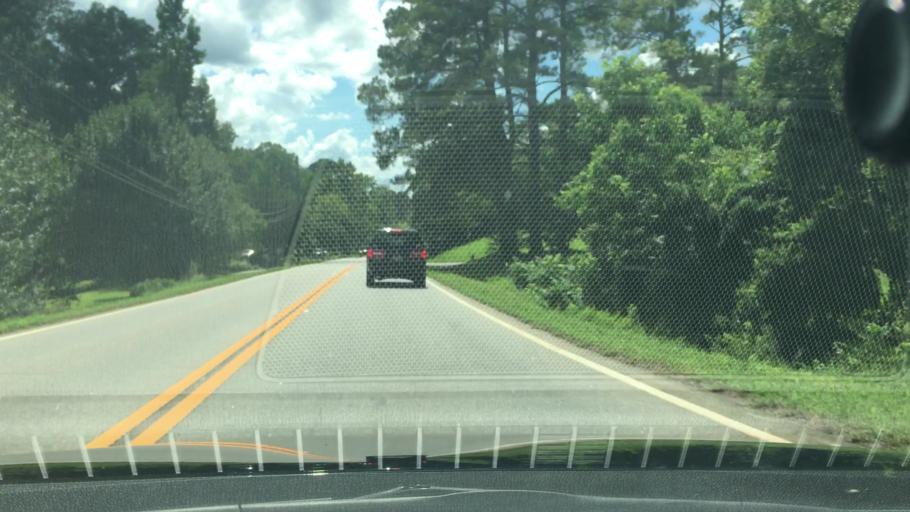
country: US
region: Georgia
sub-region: Putnam County
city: Eatonton
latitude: 33.3220
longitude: -83.4002
